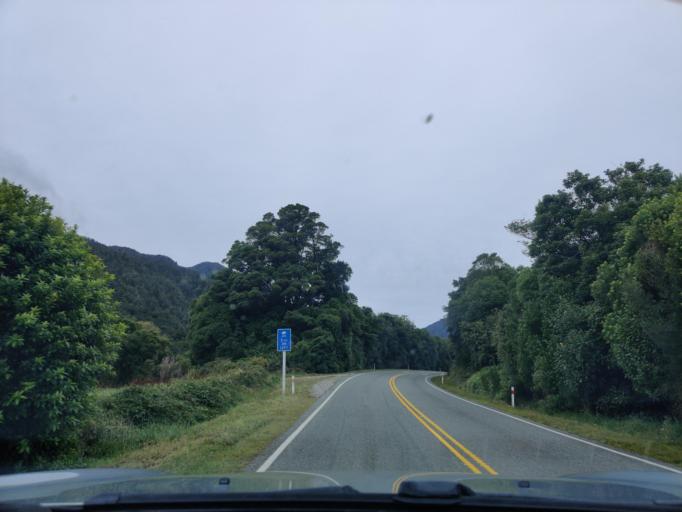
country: NZ
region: West Coast
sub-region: Buller District
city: Westport
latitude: -41.8314
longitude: 171.6536
